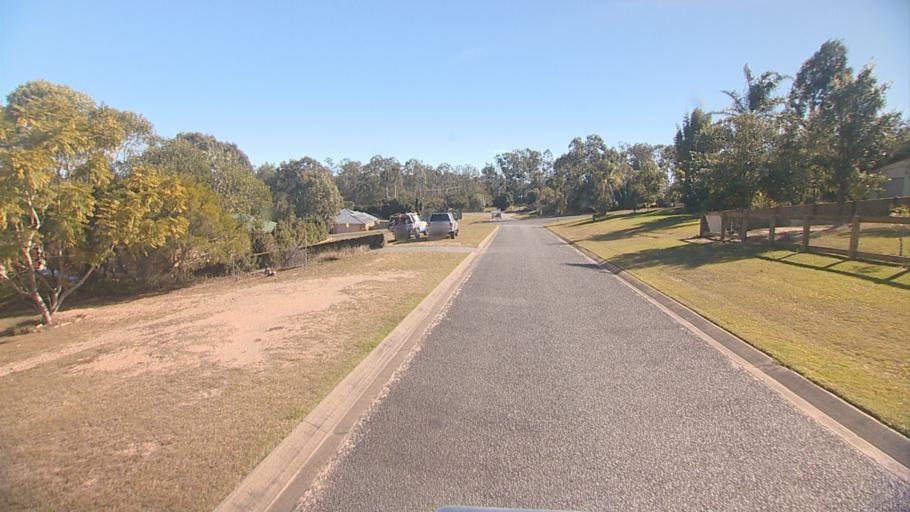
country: AU
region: Queensland
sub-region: Ipswich
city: Springfield Lakes
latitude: -27.7304
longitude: 152.9429
